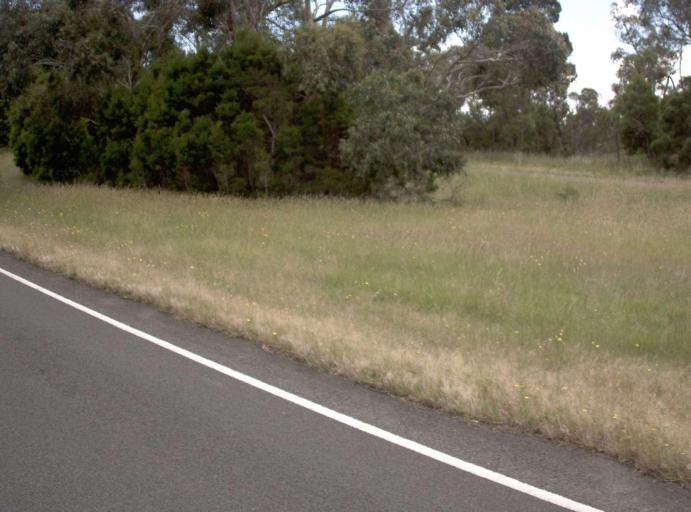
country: AU
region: Victoria
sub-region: Cardinia
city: Koo-Wee-Rup
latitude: -38.3224
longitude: 145.5409
